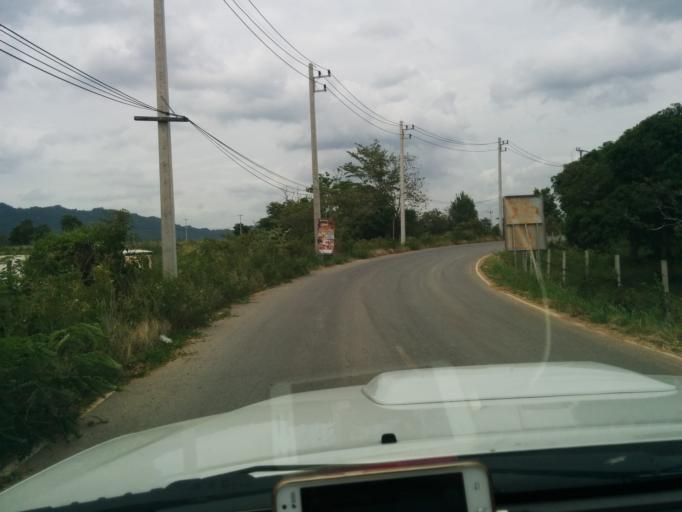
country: TH
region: Sara Buri
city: Muak Lek
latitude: 14.5661
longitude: 101.2476
